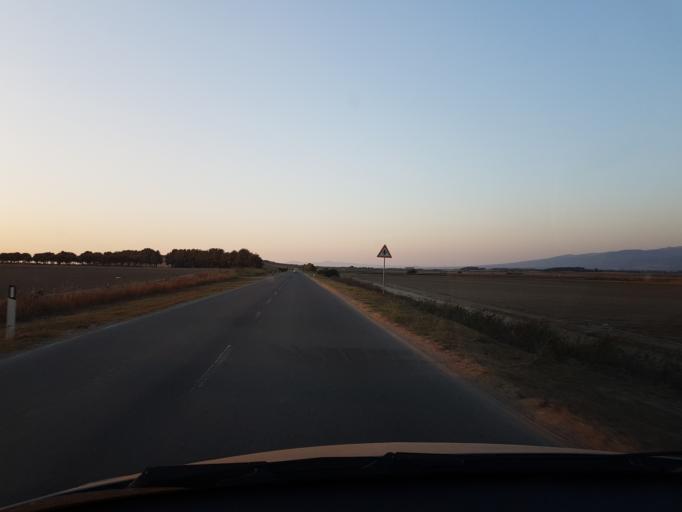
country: IT
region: Sardinia
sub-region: Provincia di Oristano
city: Nurachi
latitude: 39.9675
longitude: 8.4529
